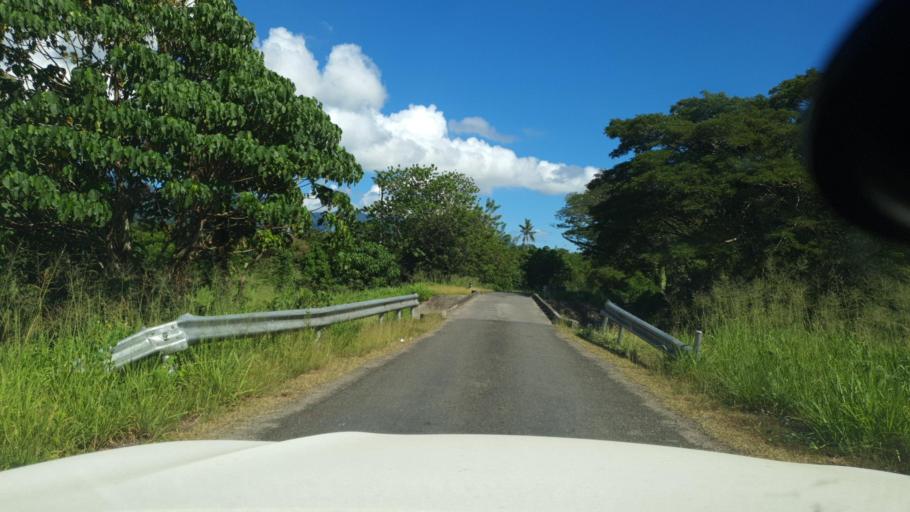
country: SB
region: Guadalcanal
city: Honiara
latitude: -9.3208
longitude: 159.8019
